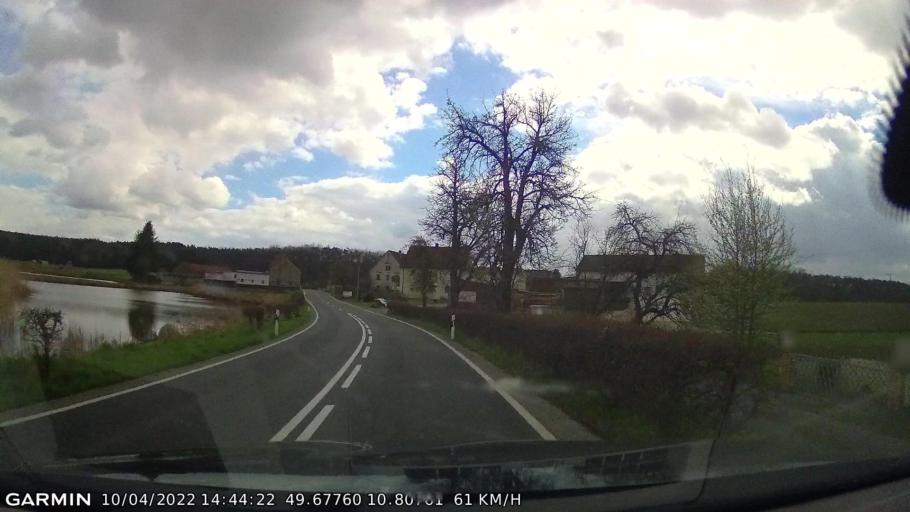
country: DE
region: Bavaria
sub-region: Regierungsbezirk Mittelfranken
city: Hochstadt an der Aisch
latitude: 49.6775
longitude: 10.8076
